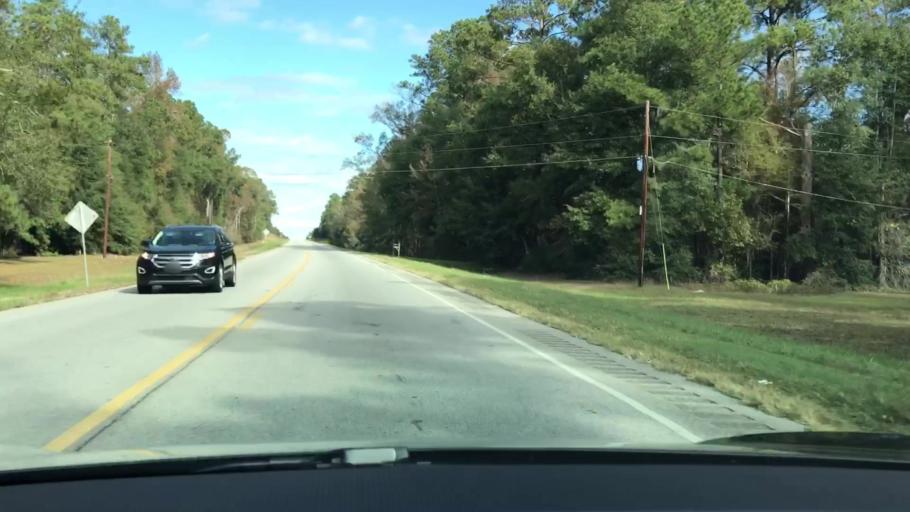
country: US
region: Georgia
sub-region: Jefferson County
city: Louisville
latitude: 32.9765
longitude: -82.3906
